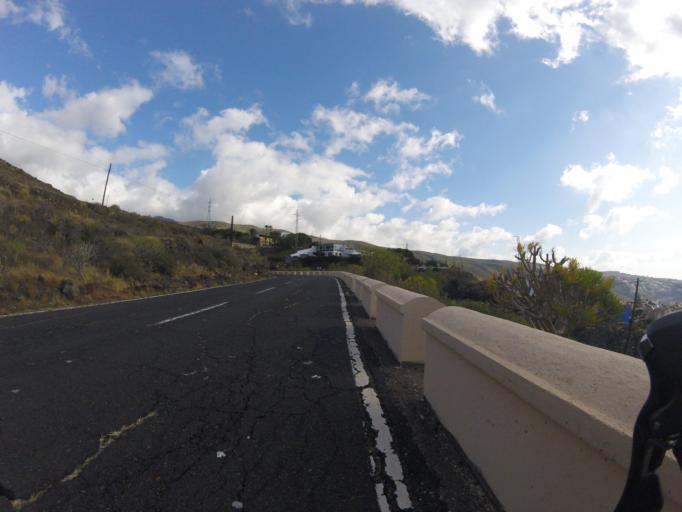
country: ES
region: Canary Islands
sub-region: Provincia de Santa Cruz de Tenerife
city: Candelaria
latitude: 28.3940
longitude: -16.3510
